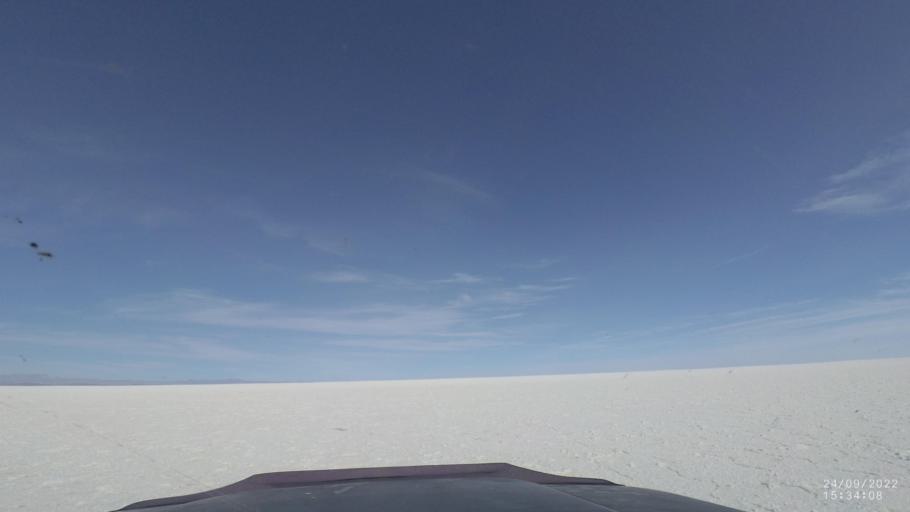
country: BO
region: Potosi
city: Colchani
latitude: -20.1215
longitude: -67.2651
